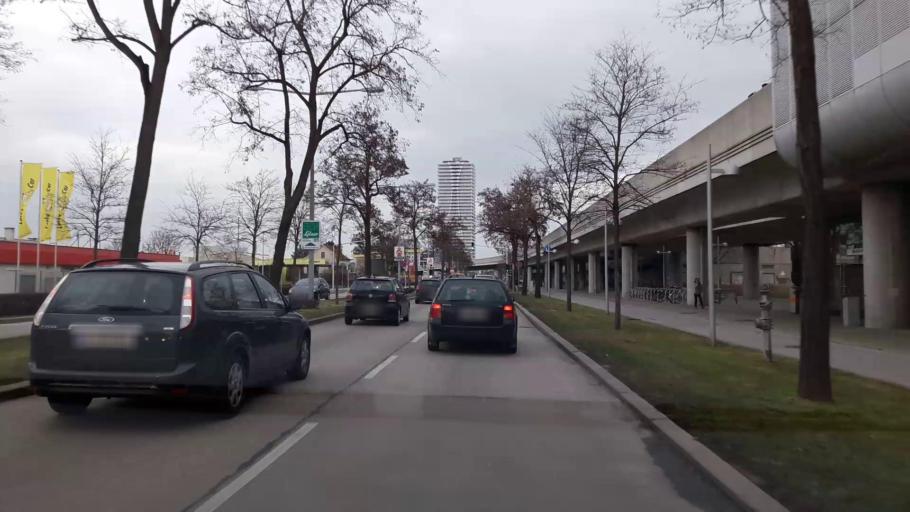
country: AT
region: Lower Austria
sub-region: Politischer Bezirk Wien-Umgebung
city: Gerasdorf bei Wien
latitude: 48.2581
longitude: 16.4498
